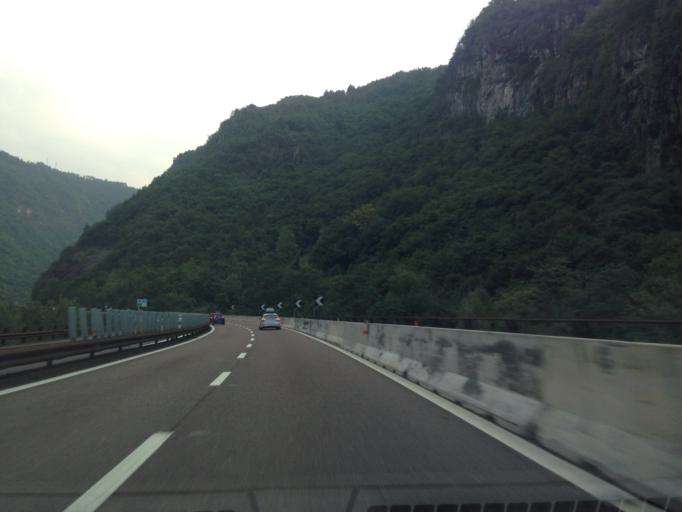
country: IT
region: Trentino-Alto Adige
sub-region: Bolzano
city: Fie Allo Sciliar
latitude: 46.5518
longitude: 11.5144
